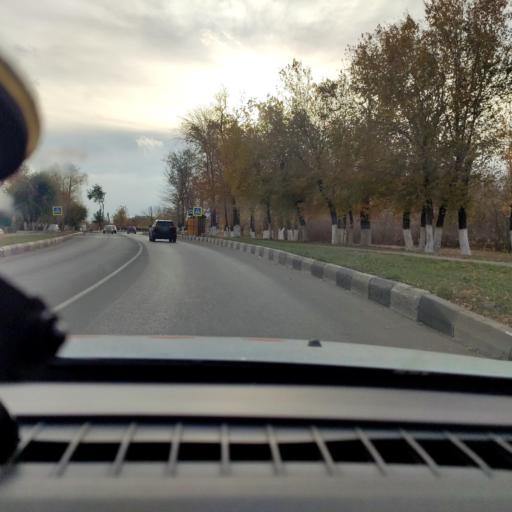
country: RU
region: Samara
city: Novokuybyshevsk
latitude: 53.1147
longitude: 49.9463
